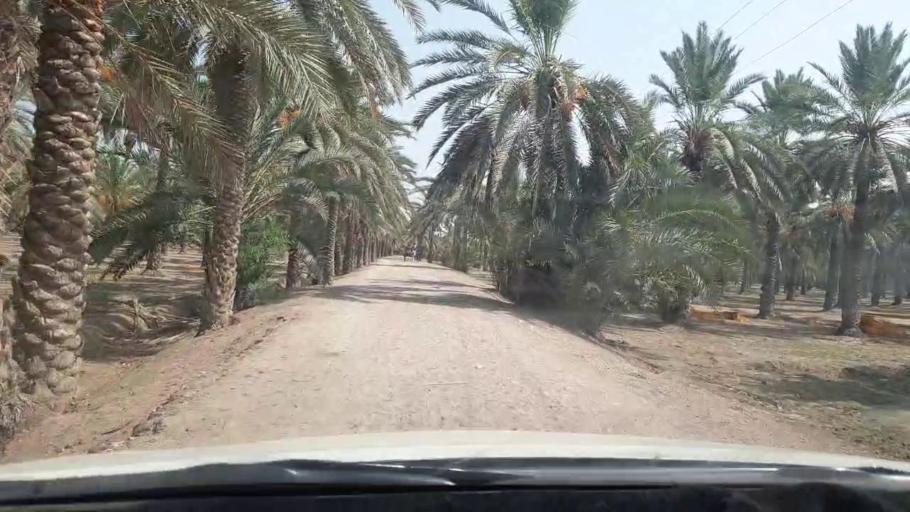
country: PK
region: Sindh
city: Rohri
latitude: 27.6265
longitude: 68.8872
